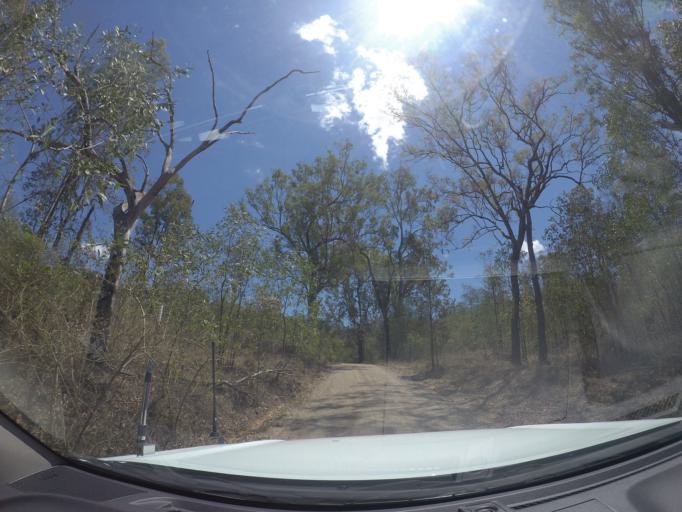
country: AU
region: Queensland
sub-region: Ipswich
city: Springfield Lakes
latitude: -27.8074
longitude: 152.8451
